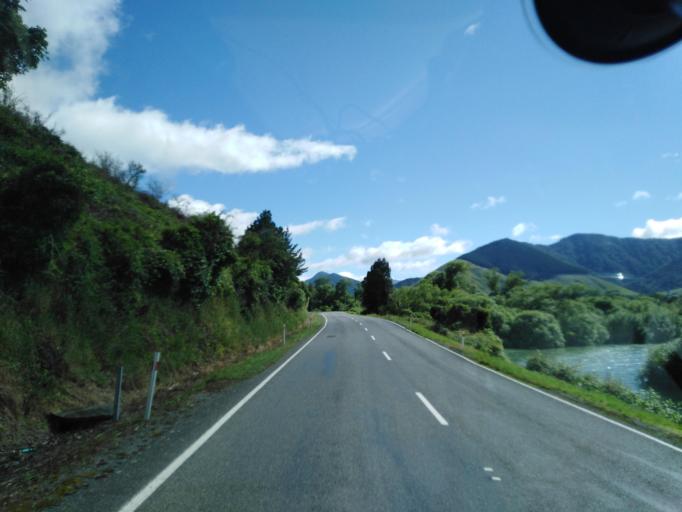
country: NZ
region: Nelson
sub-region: Nelson City
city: Nelson
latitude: -41.2551
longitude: 173.5765
